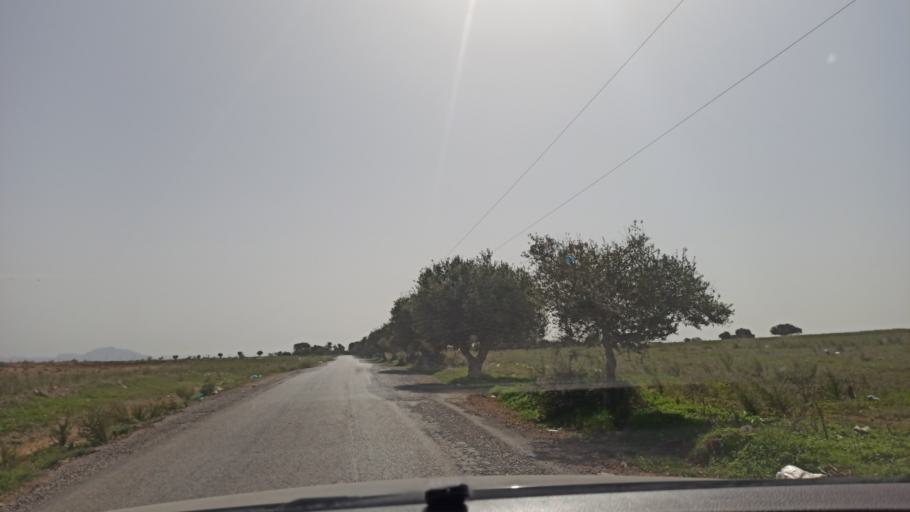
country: TN
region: Manouba
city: Manouba
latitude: 36.7351
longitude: 10.0856
